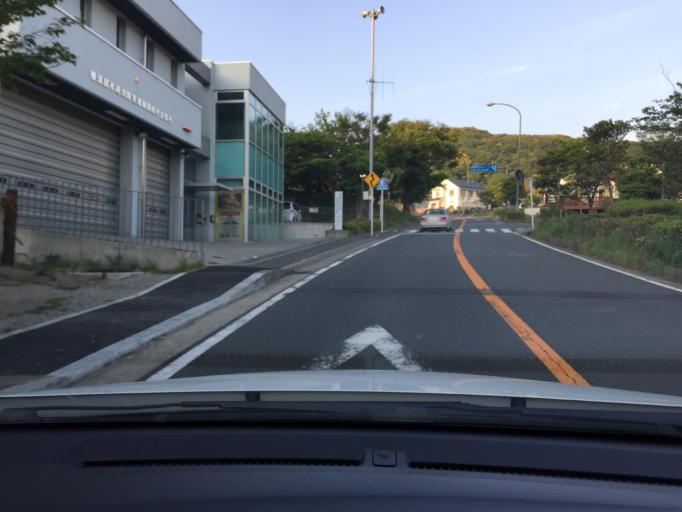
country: JP
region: Kanagawa
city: Hayama
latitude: 35.2507
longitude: 139.6052
